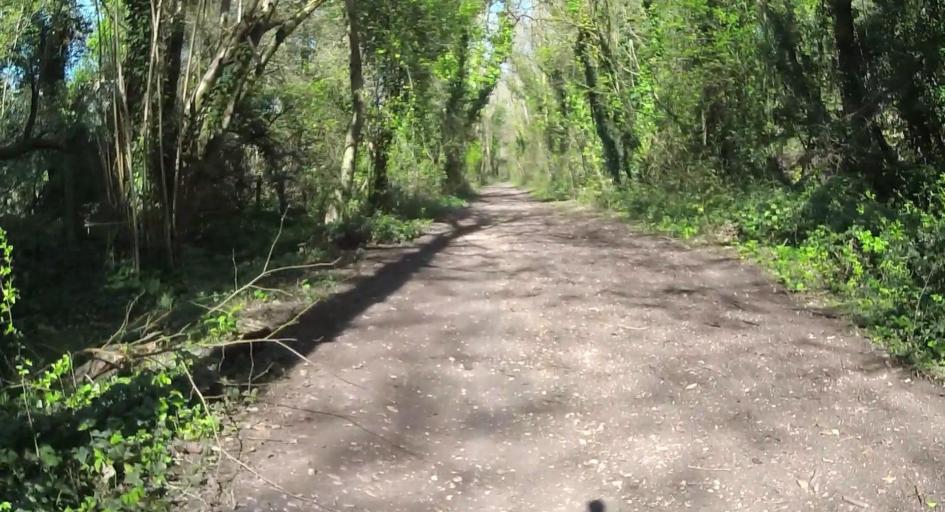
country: GB
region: England
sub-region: Hampshire
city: Romsey
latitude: 51.0767
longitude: -1.5055
